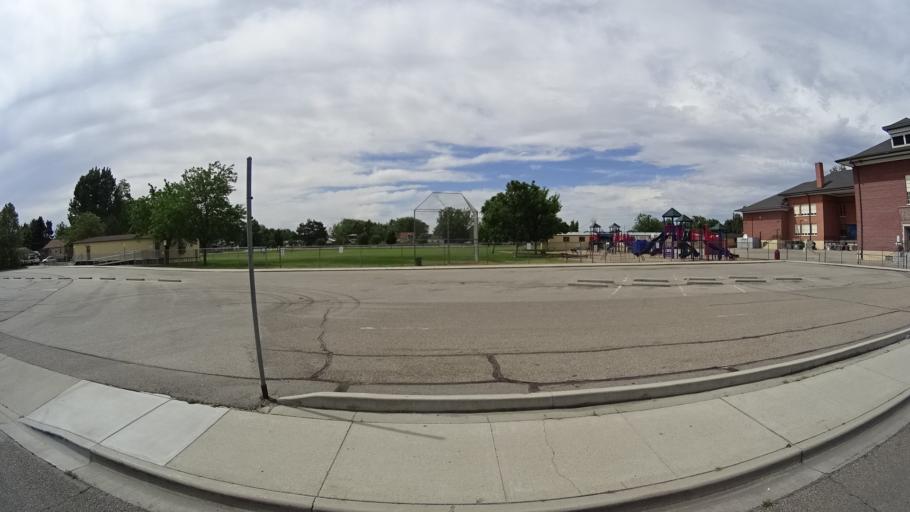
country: US
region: Idaho
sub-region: Ada County
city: Boise
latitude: 43.5895
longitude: -116.1920
